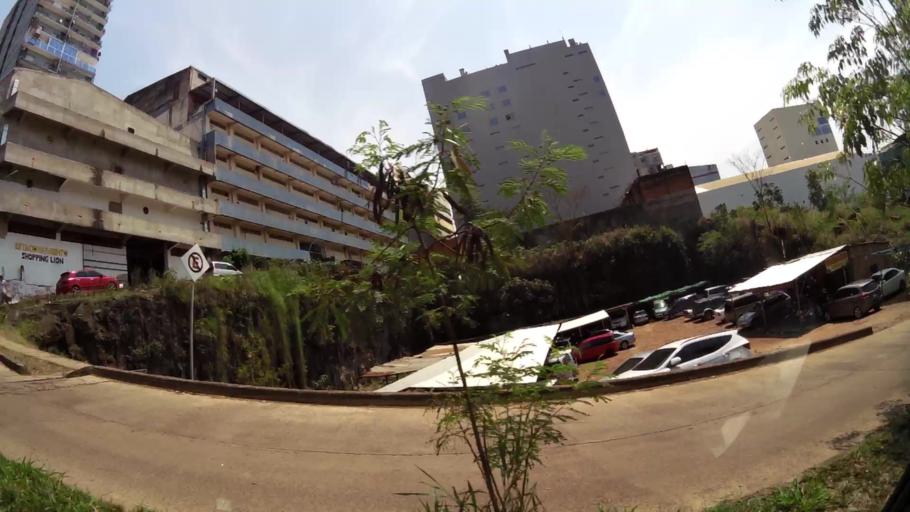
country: PY
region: Alto Parana
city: Ciudad del Este
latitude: -25.5130
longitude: -54.6084
